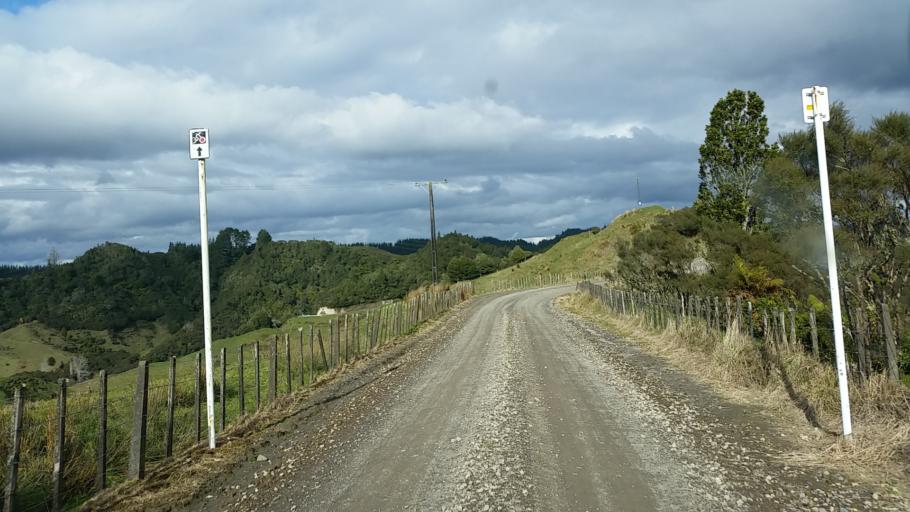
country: NZ
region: Taranaki
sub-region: South Taranaki District
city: Eltham
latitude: -39.1718
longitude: 174.6265
